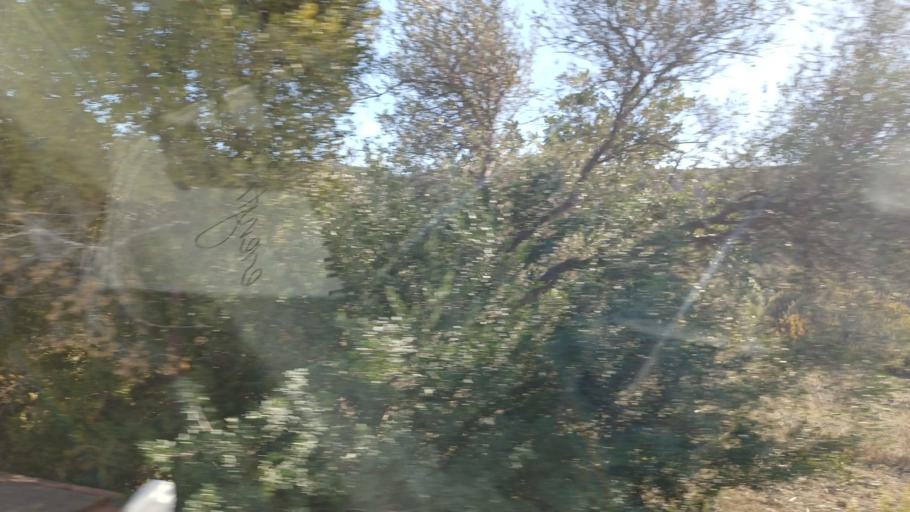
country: CY
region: Limassol
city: Pyrgos
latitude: 34.7803
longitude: 33.2489
